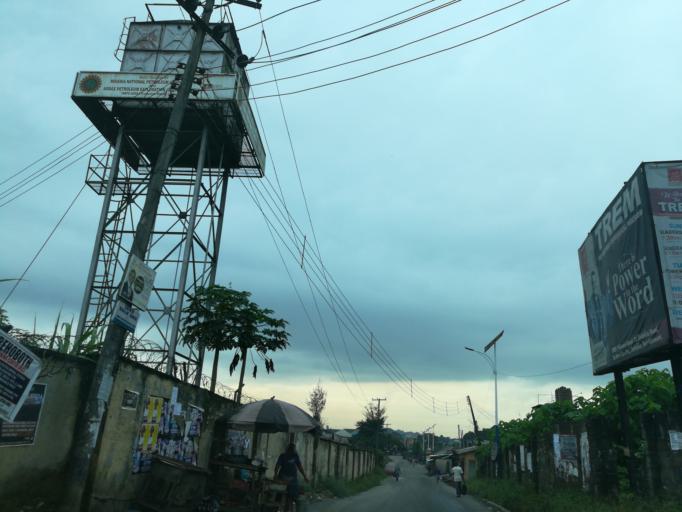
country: NG
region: Rivers
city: Port Harcourt
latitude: 4.8143
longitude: 7.0216
